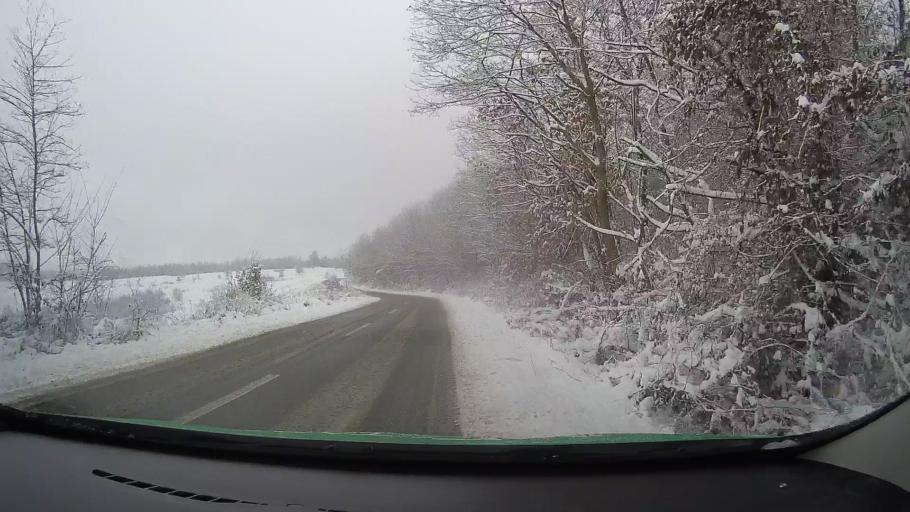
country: RO
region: Hunedoara
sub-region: Comuna Teliucu Inferior
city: Teliucu Inferior
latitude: 45.6843
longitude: 22.9099
